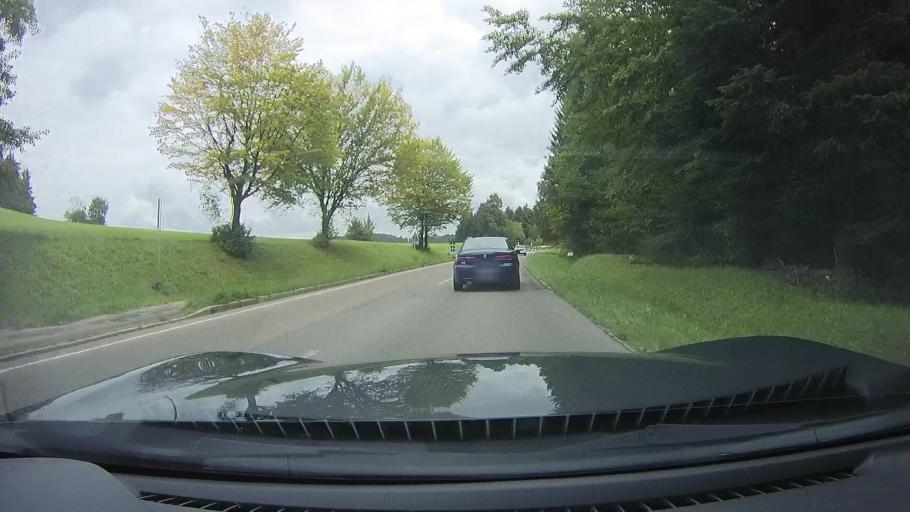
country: DE
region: Baden-Wuerttemberg
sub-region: Regierungsbezirk Stuttgart
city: Althutte
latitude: 48.9240
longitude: 9.5925
